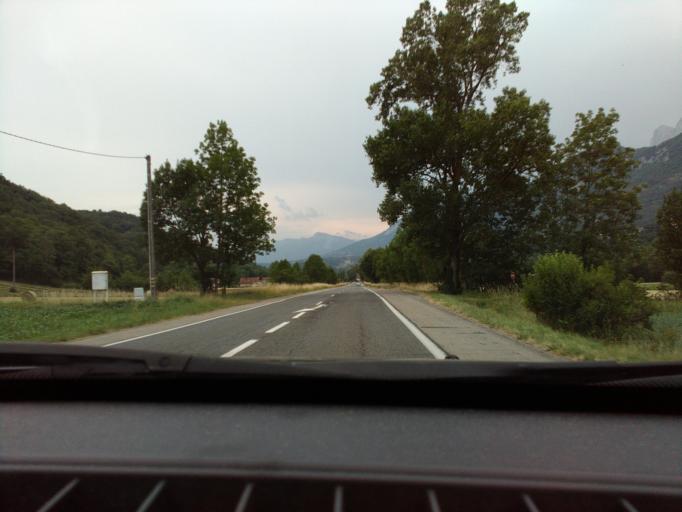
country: FR
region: Rhone-Alpes
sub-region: Departement de l'Isere
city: Vif
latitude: 45.0372
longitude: 5.6596
